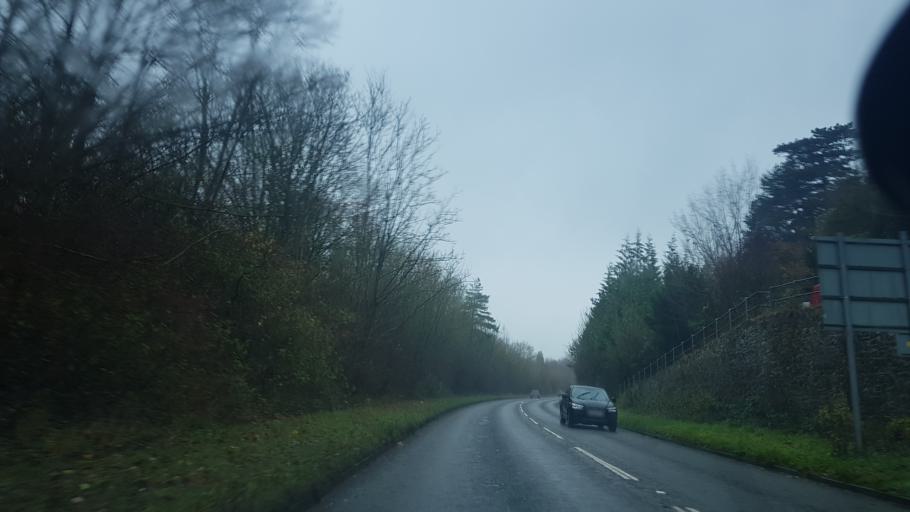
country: GB
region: England
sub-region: Surrey
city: East Horsley
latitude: 51.2595
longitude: -0.4560
